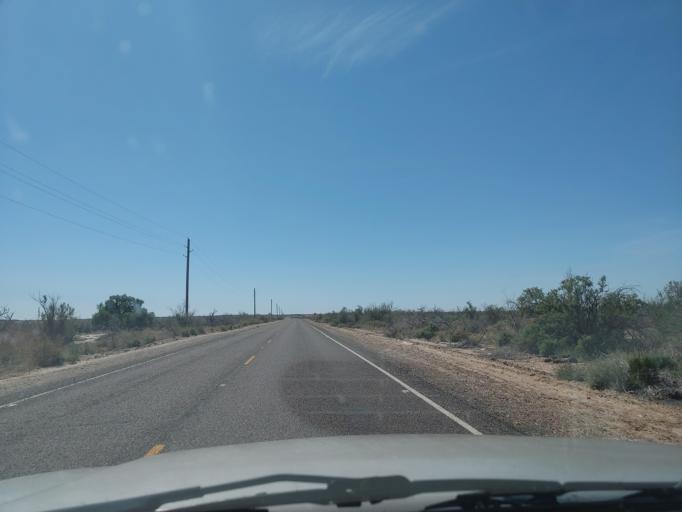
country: US
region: Arizona
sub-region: Maricopa County
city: Gila Bend
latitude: 32.9750
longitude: -113.3060
